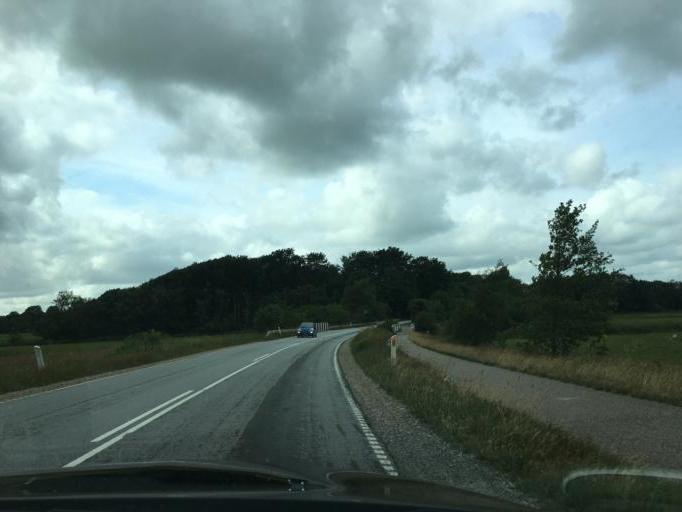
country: DK
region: South Denmark
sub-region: Esbjerg Kommune
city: Bramming
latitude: 55.4957
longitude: 8.6969
